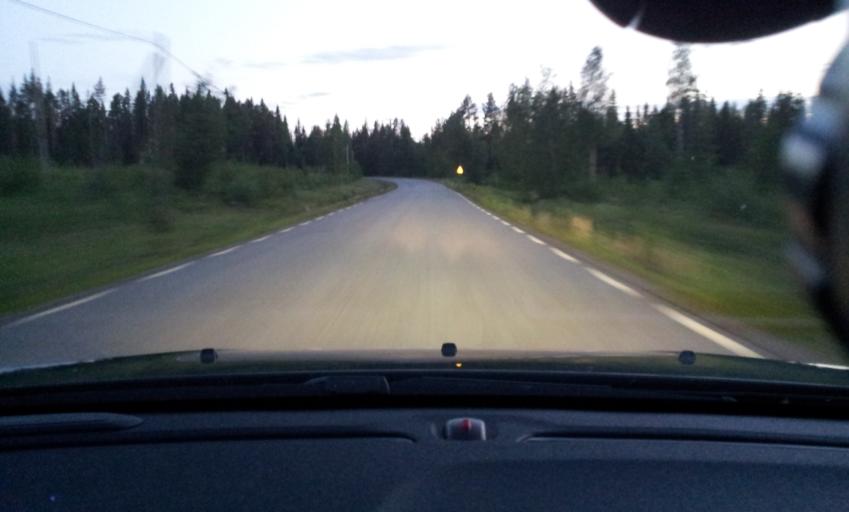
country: SE
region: Jaemtland
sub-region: Braecke Kommun
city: Braecke
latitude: 62.7641
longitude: 15.3034
